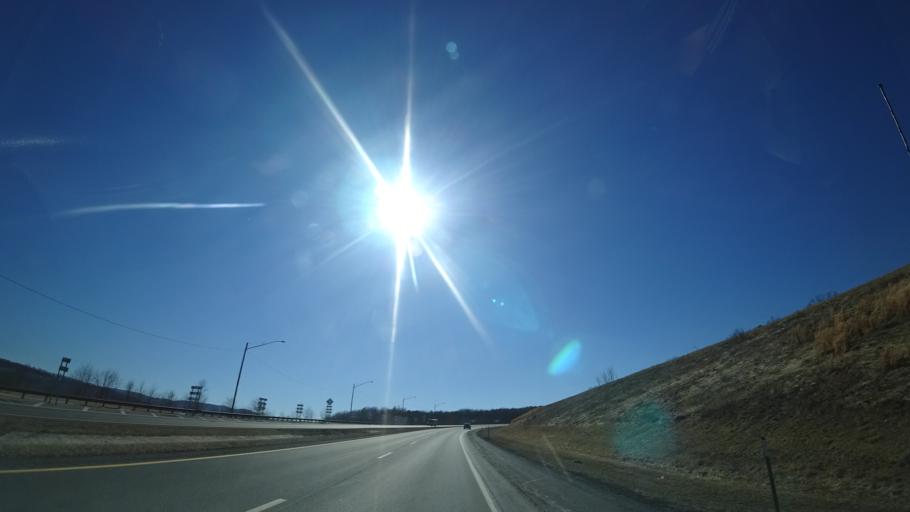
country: US
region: Virginia
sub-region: Shenandoah County
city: Woodstock
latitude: 39.0727
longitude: -78.6296
